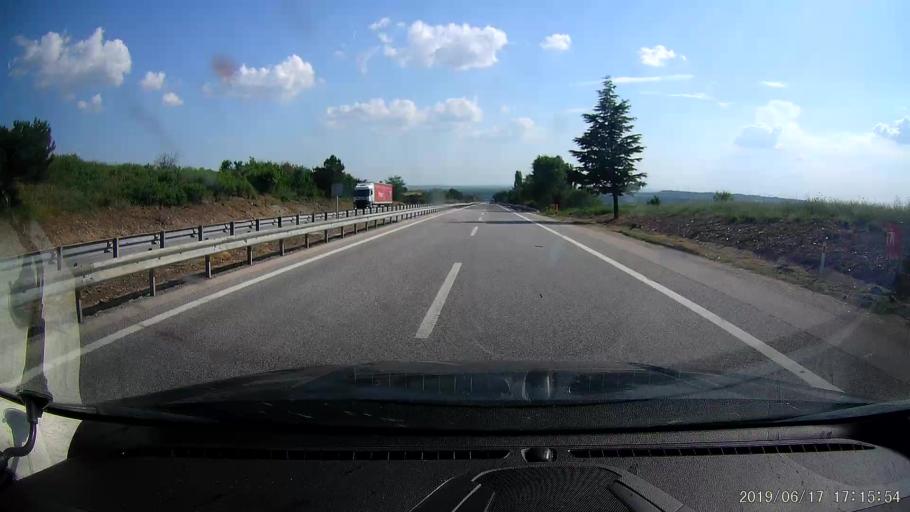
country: GR
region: East Macedonia and Thrace
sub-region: Nomos Evrou
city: Kastanies
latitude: 41.6995
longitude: 26.4875
